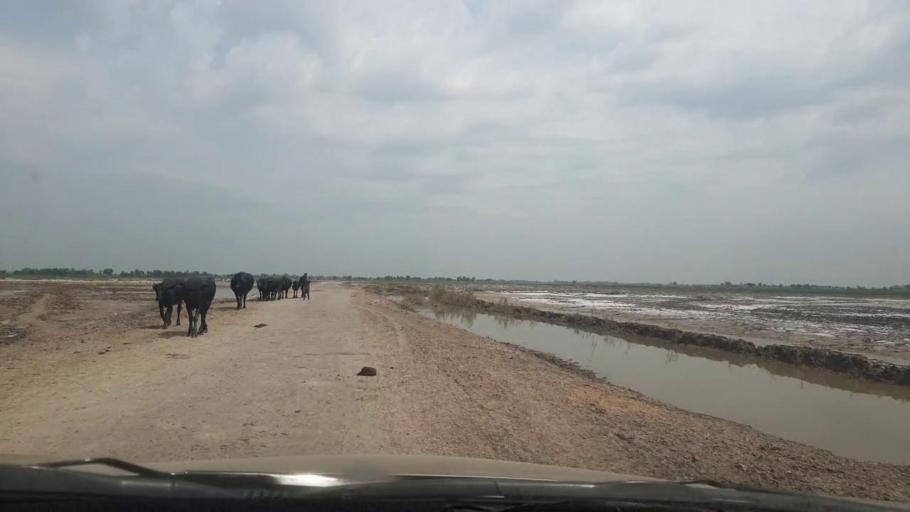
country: PK
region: Sindh
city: Ratodero
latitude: 27.7065
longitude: 68.2288
